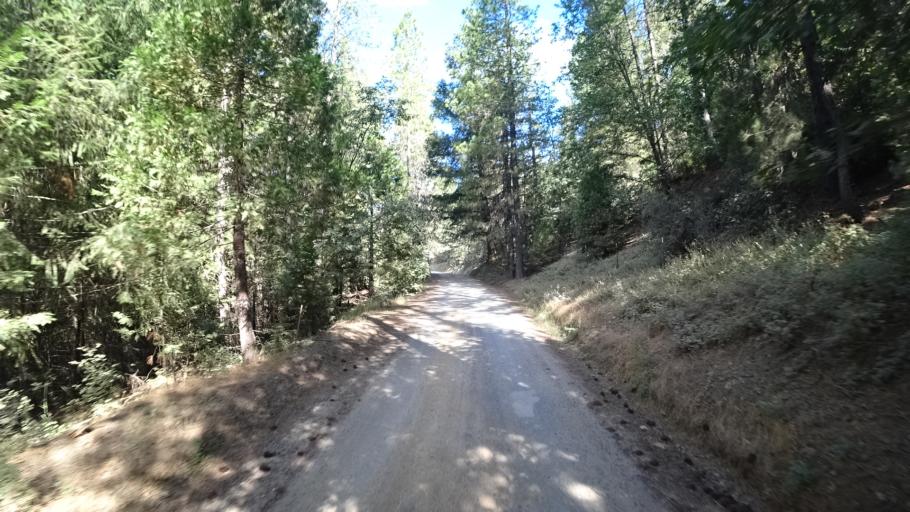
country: US
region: California
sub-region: Calaveras County
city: Arnold
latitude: 38.3674
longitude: -120.4389
